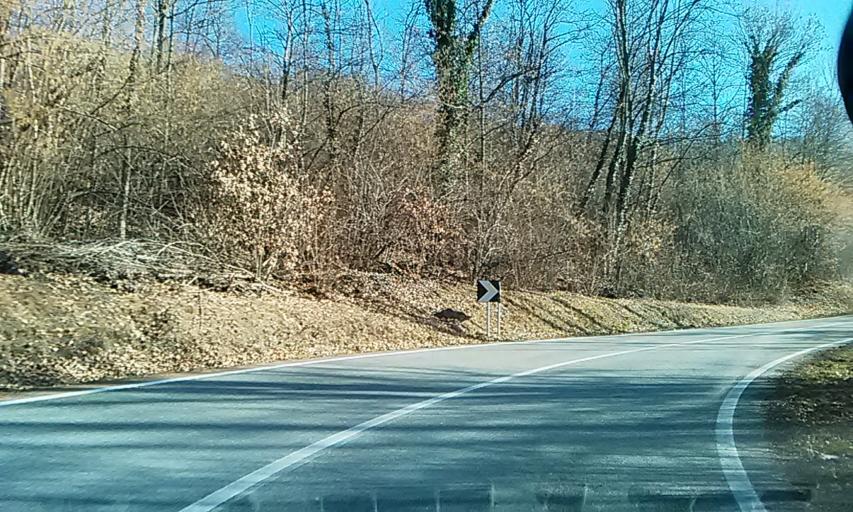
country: IT
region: Piedmont
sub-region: Provincia di Vercelli
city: Cellio
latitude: 45.7475
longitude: 8.3103
